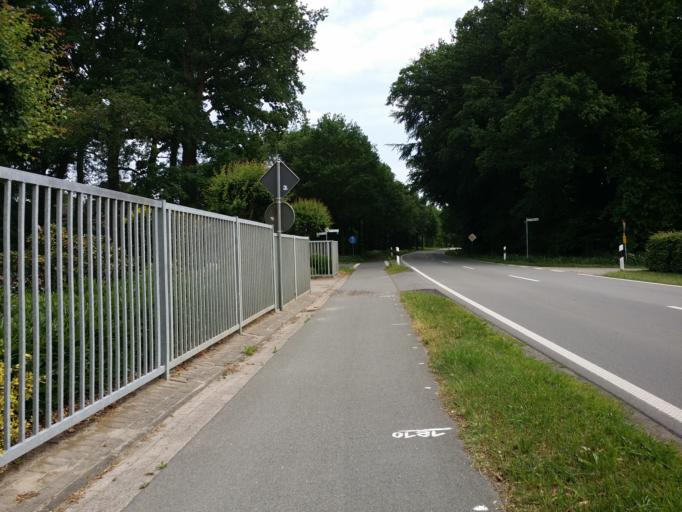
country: DE
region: Lower Saxony
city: Rastede
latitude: 53.2360
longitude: 8.1671
